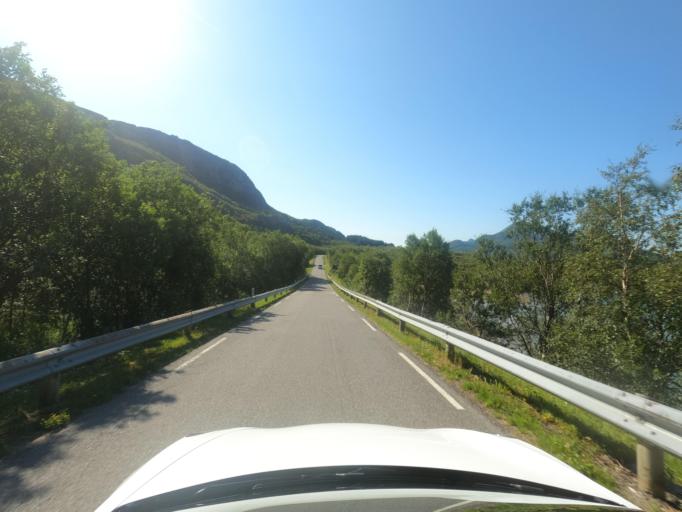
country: NO
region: Nordland
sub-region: Hadsel
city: Stokmarknes
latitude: 68.3236
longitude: 15.0062
